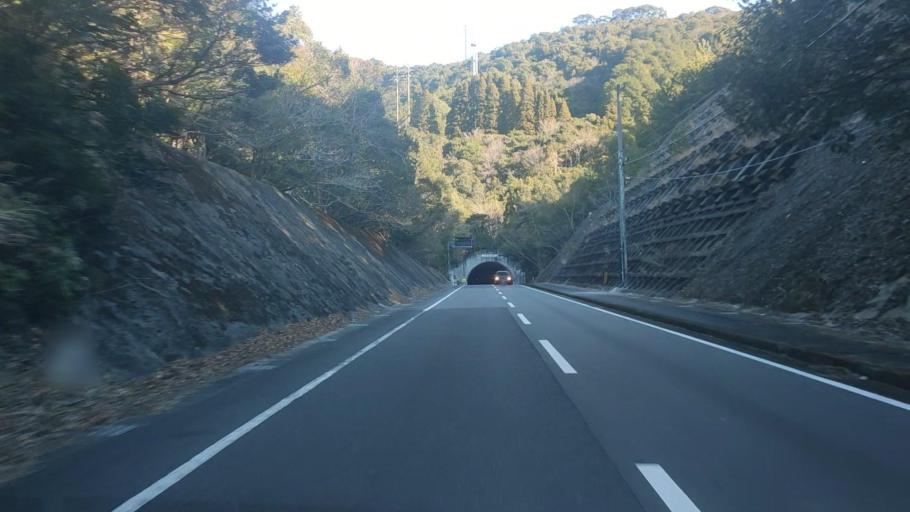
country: JP
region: Miyazaki
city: Nobeoka
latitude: 32.6697
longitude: 131.7670
